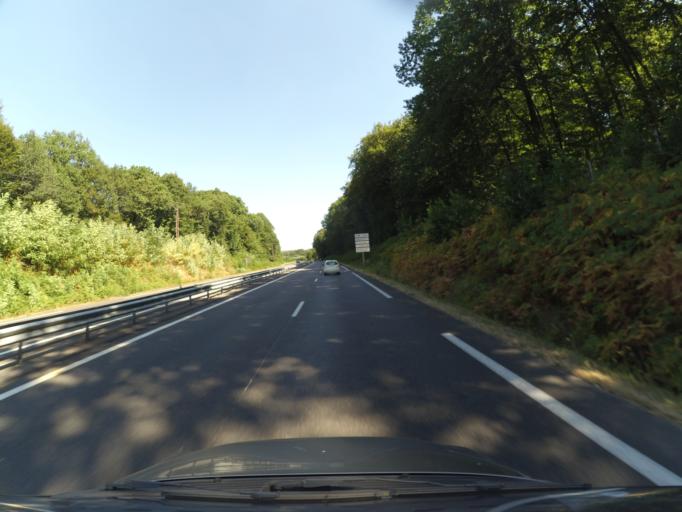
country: FR
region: Limousin
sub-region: Departement de la Haute-Vienne
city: Isle
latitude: 45.8406
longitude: 1.1824
